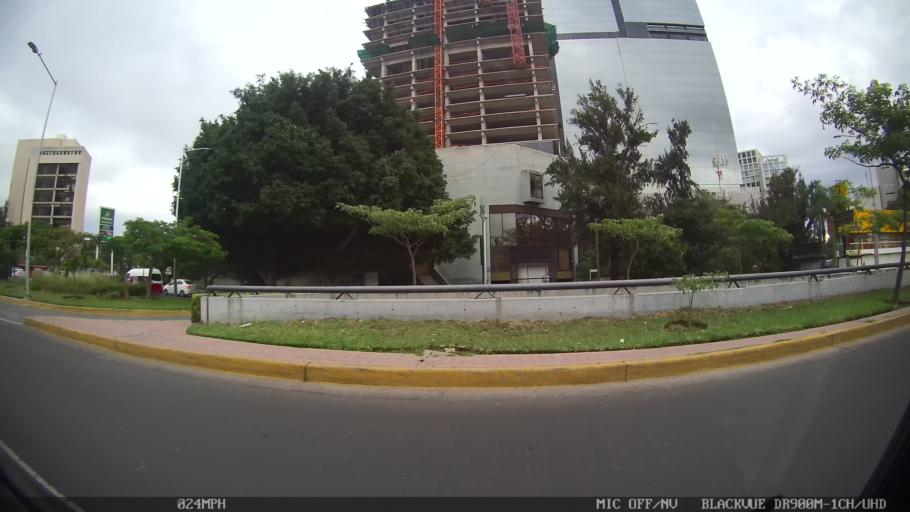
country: MX
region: Jalisco
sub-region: Zapopan
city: Zapopan
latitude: 20.6962
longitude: -103.3725
